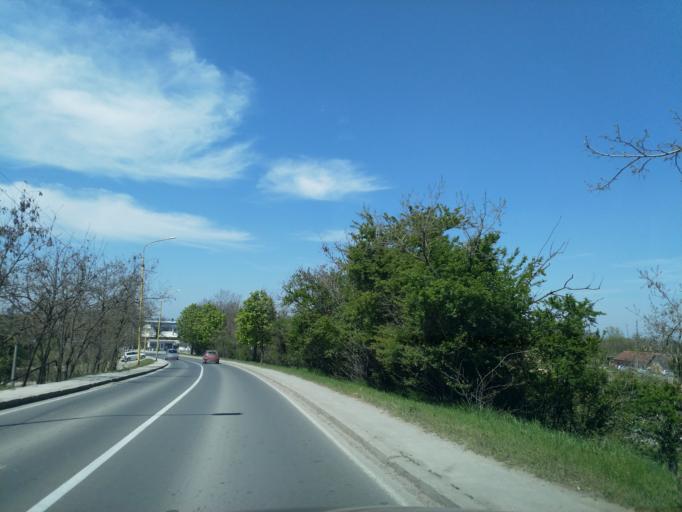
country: RS
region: Central Serbia
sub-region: Belgrade
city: Lazarevac
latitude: 44.3870
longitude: 20.2474
